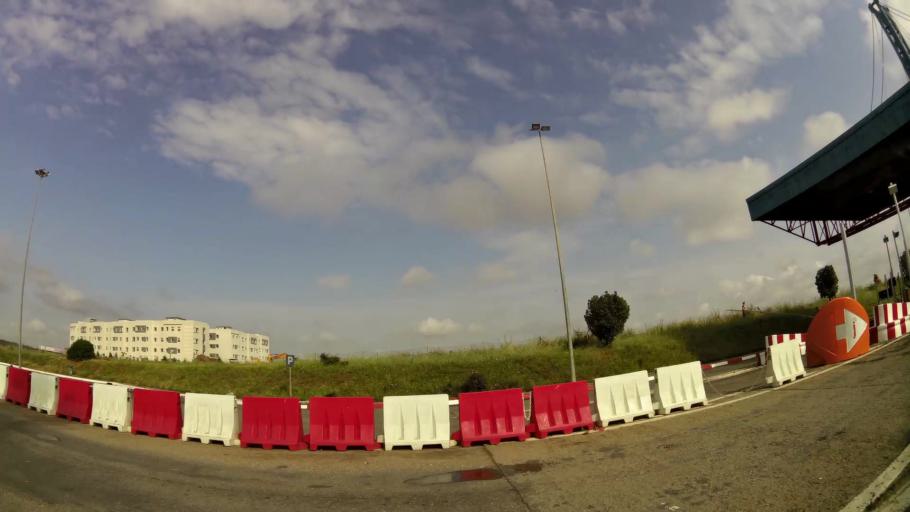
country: MA
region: Rabat-Sale-Zemmour-Zaer
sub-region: Khemisset
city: Tiflet
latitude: 33.8811
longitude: -6.3226
